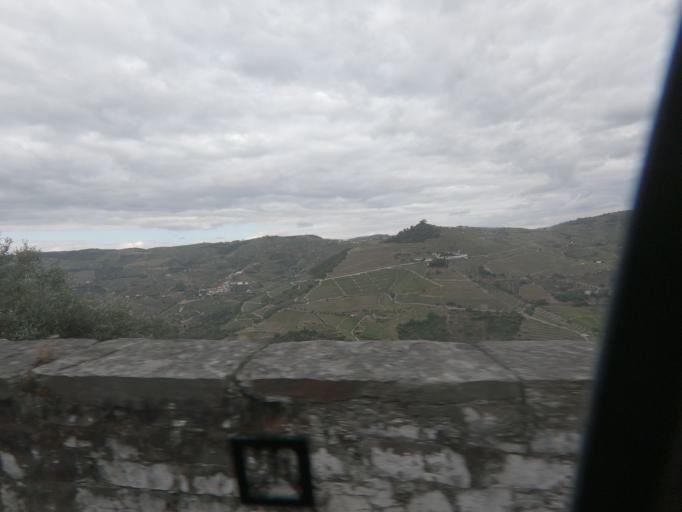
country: PT
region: Vila Real
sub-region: Sabrosa
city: Vilela
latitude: 41.2155
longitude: -7.5524
